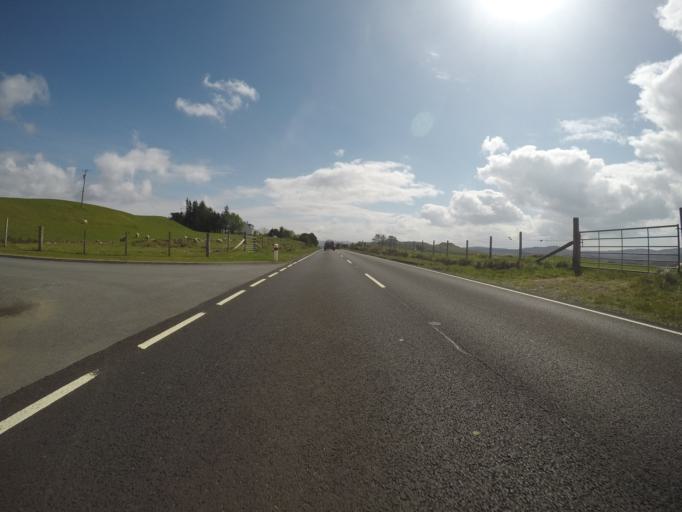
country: GB
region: Scotland
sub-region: Highland
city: Portree
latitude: 57.4948
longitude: -6.3208
